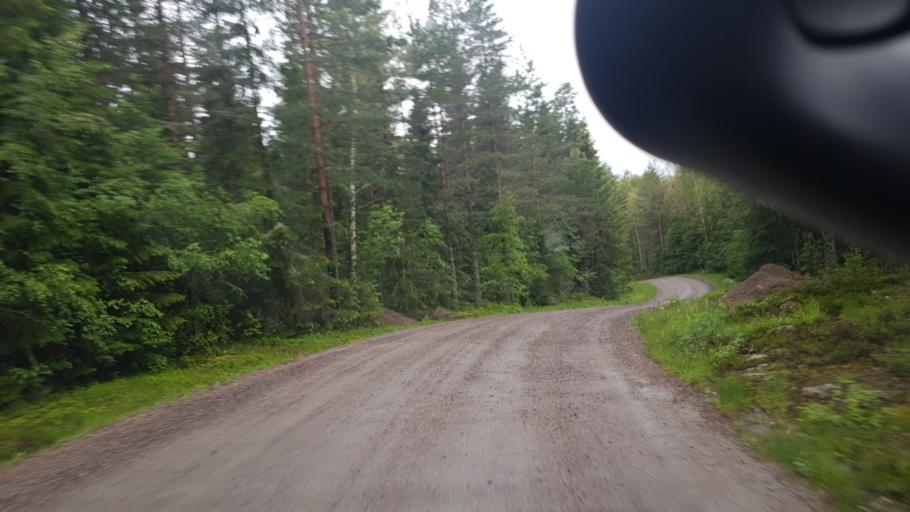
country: SE
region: Vaermland
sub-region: Eda Kommun
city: Charlottenberg
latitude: 59.7294
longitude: 12.1170
